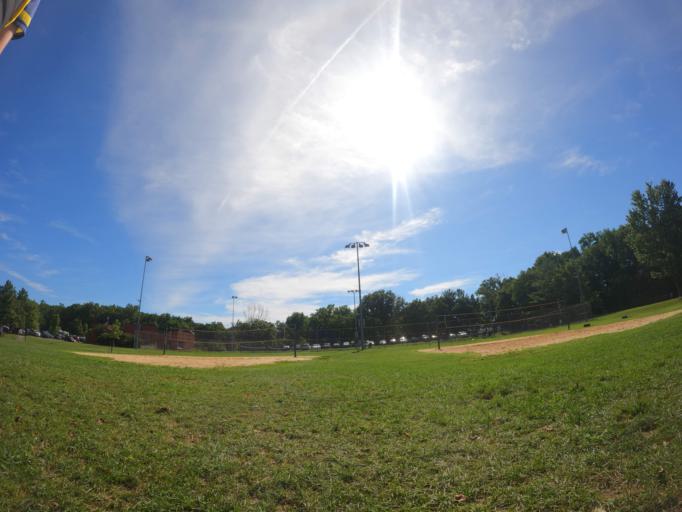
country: US
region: Maryland
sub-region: Howard County
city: Savage
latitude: 39.1388
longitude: -76.8299
